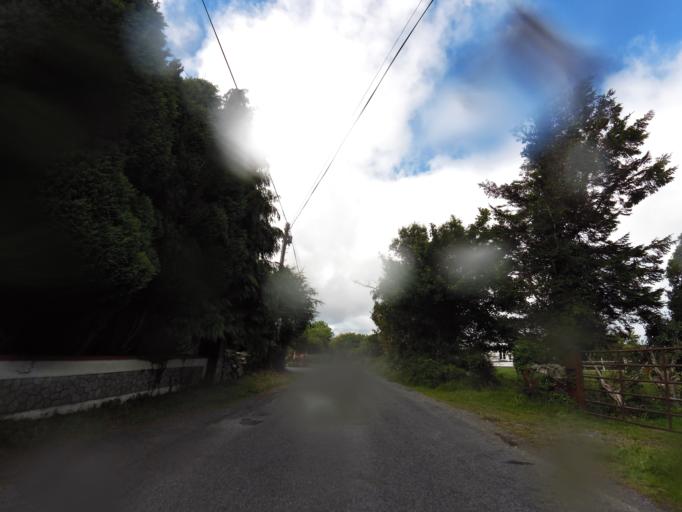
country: IE
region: Connaught
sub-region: County Galway
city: Oughterard
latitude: 53.4126
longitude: -9.3305
